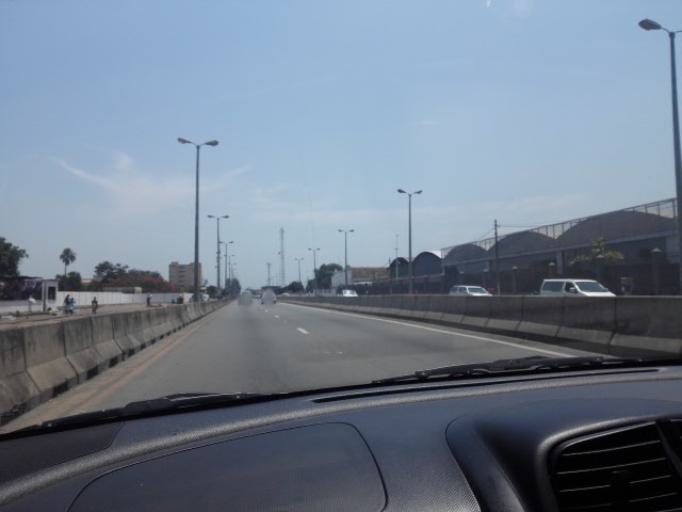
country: MZ
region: Maputo City
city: Maputo
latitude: -25.9393
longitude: 32.5459
